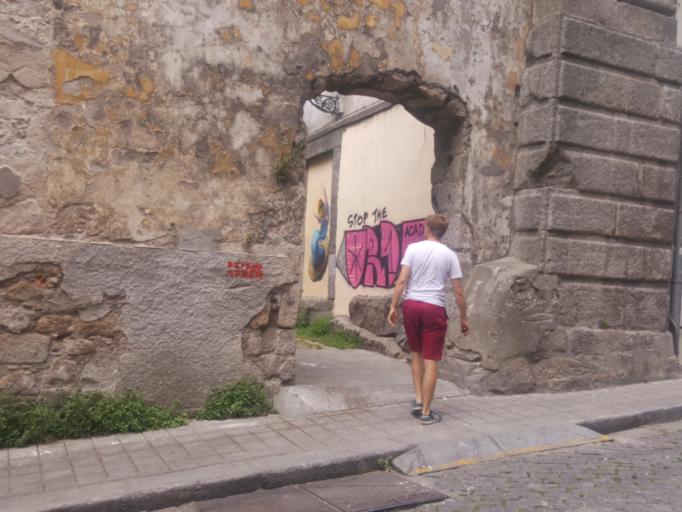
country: PT
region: Porto
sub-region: Porto
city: Porto
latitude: 41.1436
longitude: -8.6158
